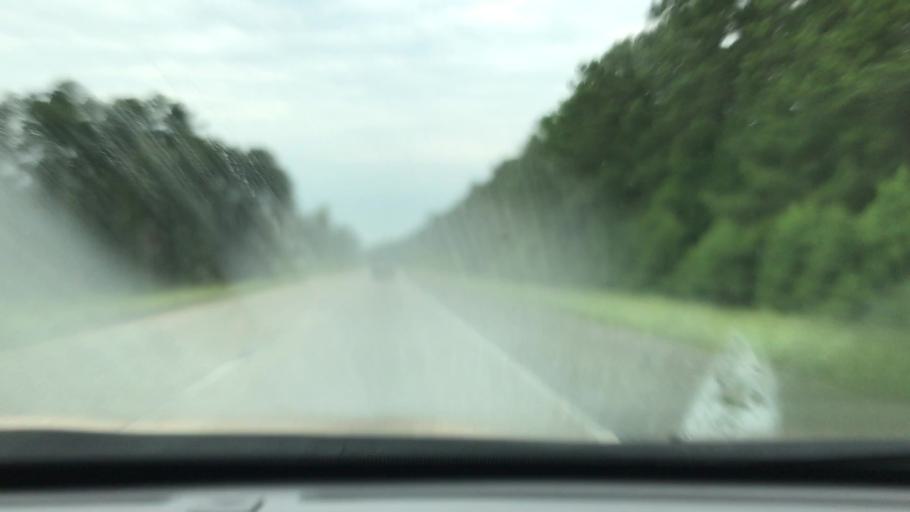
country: US
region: South Carolina
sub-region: Colleton County
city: Walterboro
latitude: 32.8652
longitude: -80.7252
